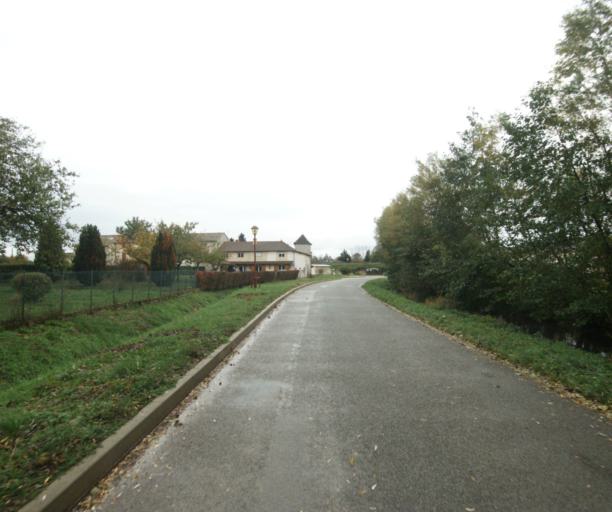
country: FR
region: Rhone-Alpes
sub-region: Departement de l'Ain
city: Pont-de-Vaux
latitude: 46.4748
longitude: 4.8950
